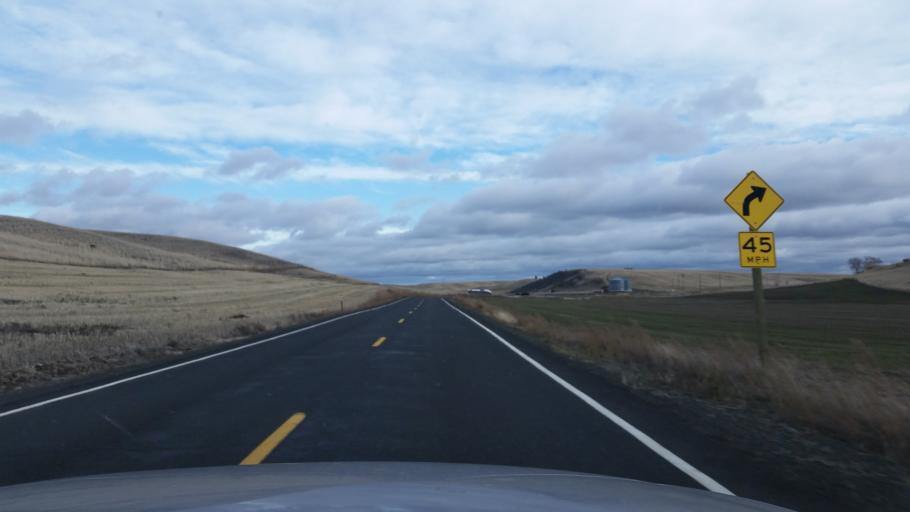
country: US
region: Washington
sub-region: Lincoln County
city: Davenport
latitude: 47.3584
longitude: -118.0449
